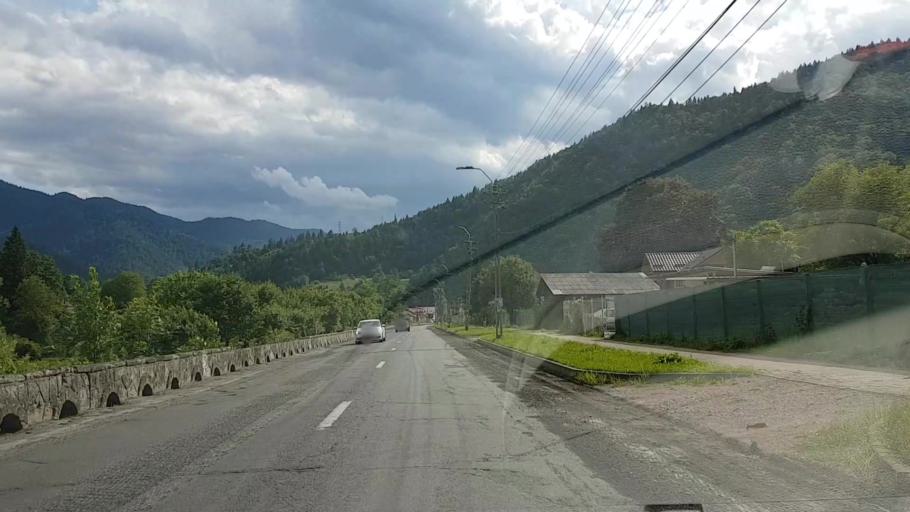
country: RO
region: Neamt
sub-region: Comuna Bicaz
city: Dodeni
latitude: 46.9233
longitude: 26.0914
